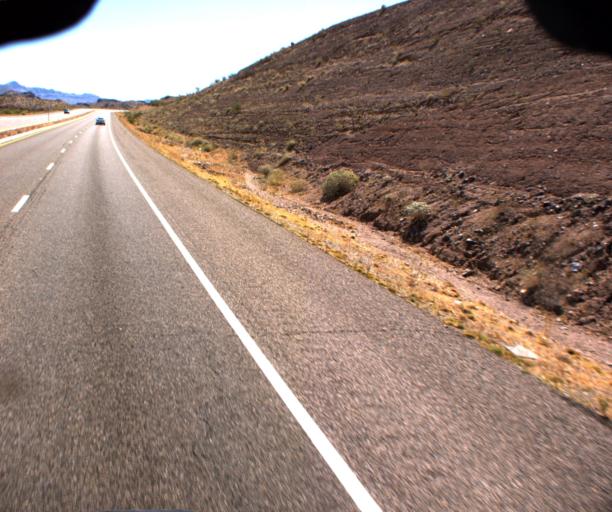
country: US
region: Nevada
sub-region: Clark County
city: Laughlin
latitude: 35.1909
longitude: -114.5238
